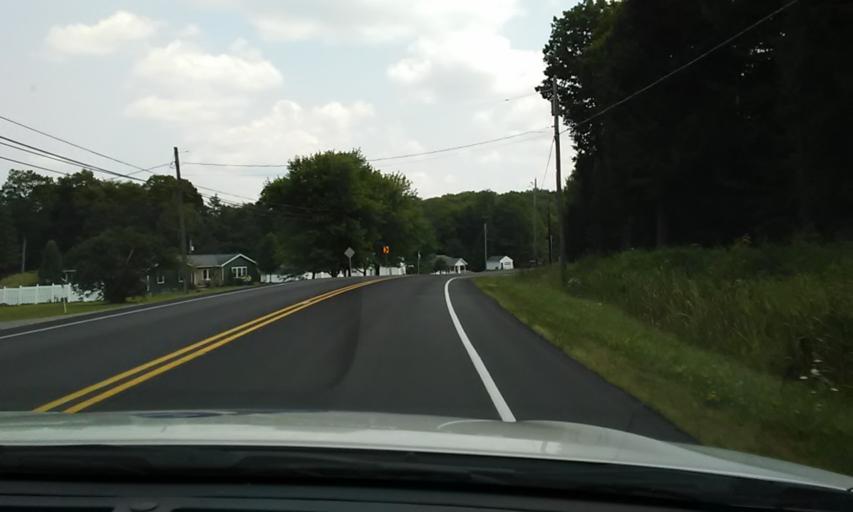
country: US
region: Pennsylvania
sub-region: Elk County
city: Saint Marys
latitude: 41.4450
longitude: -78.4977
